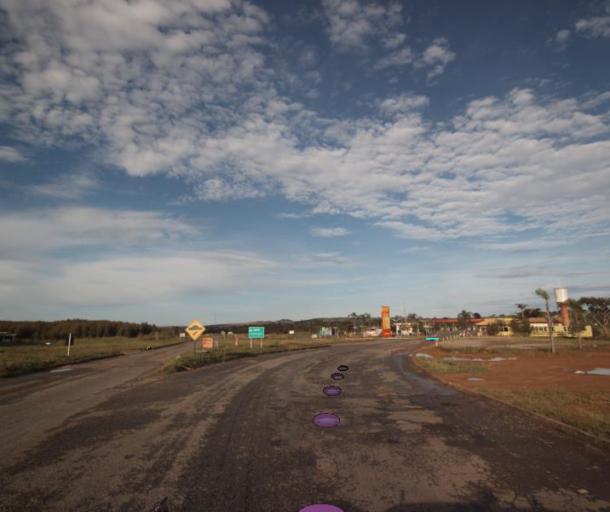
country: BR
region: Goias
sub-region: Pirenopolis
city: Pirenopolis
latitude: -15.7541
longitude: -48.7504
